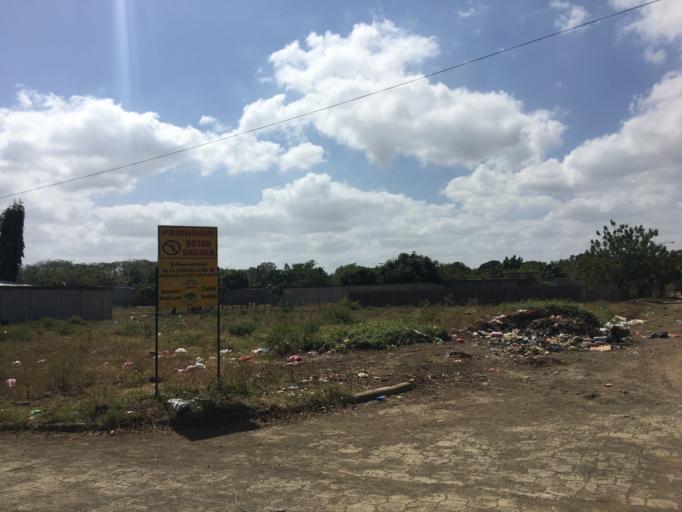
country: NI
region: Managua
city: Ciudad Sandino
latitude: 12.1641
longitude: -86.3596
